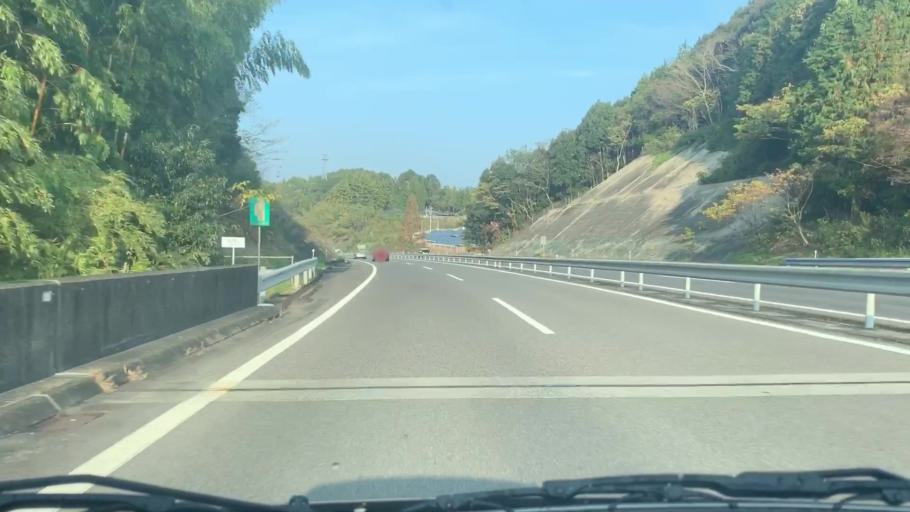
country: JP
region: Saga Prefecture
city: Ureshinomachi-shimojuku
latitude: 33.1530
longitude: 129.9335
